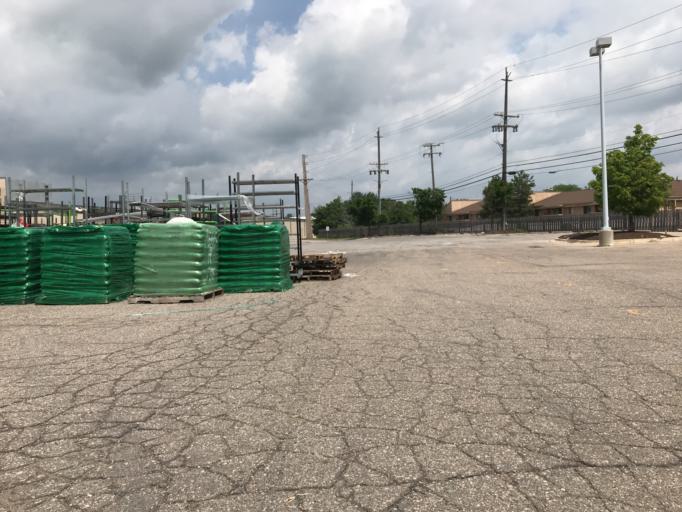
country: US
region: Michigan
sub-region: Oakland County
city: Bingham Farms
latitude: 42.4989
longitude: -83.2812
